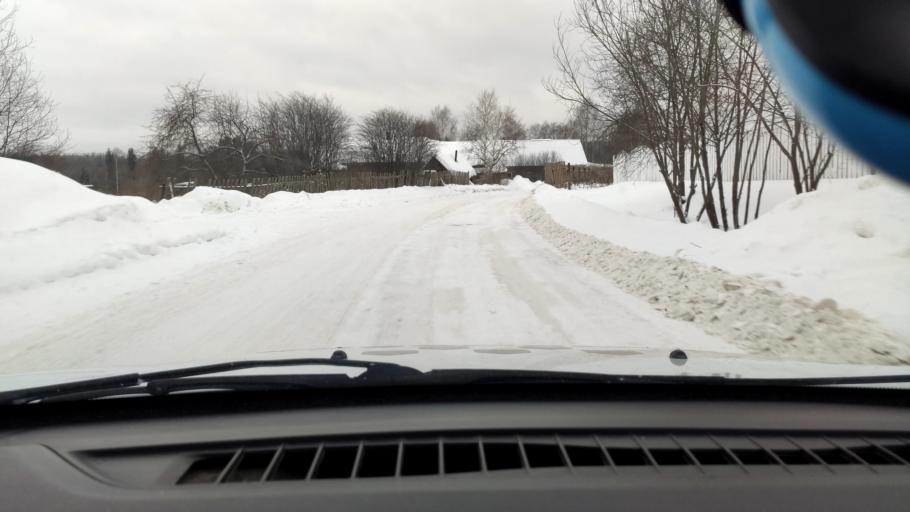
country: RU
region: Perm
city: Overyata
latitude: 58.0808
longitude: 55.9679
